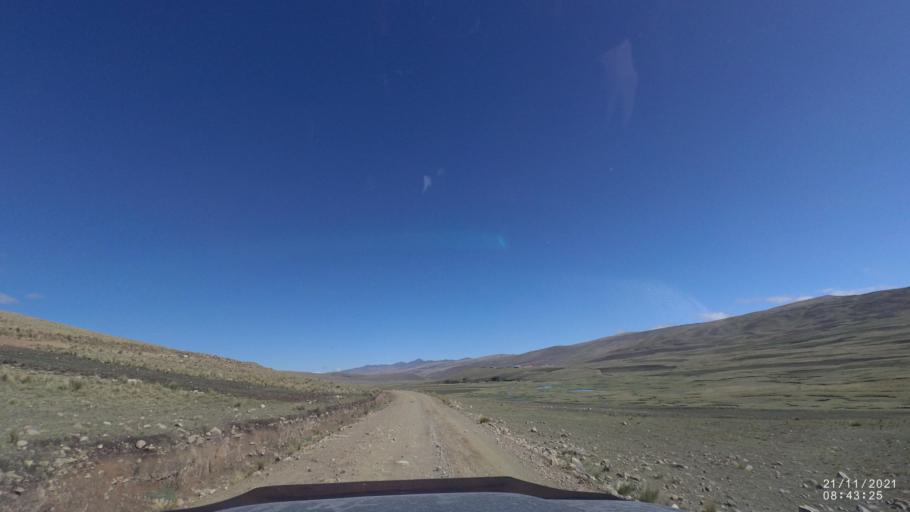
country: BO
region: Cochabamba
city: Cochabamba
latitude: -17.2605
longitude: -66.2243
